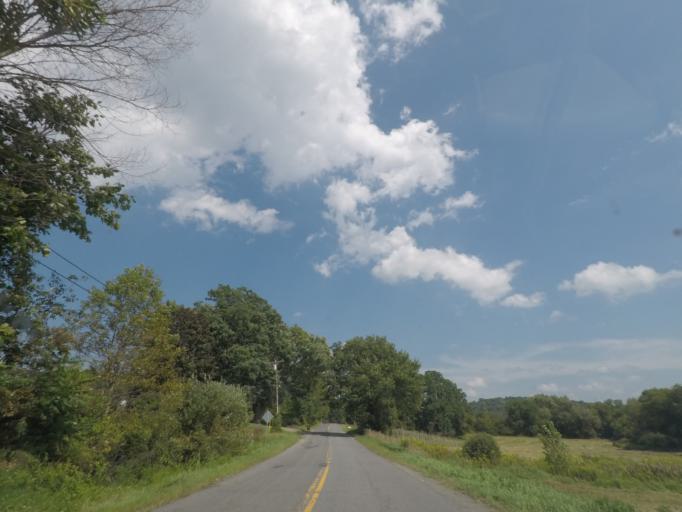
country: US
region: New York
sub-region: Saratoga County
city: Waterford
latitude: 42.8126
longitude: -73.6040
